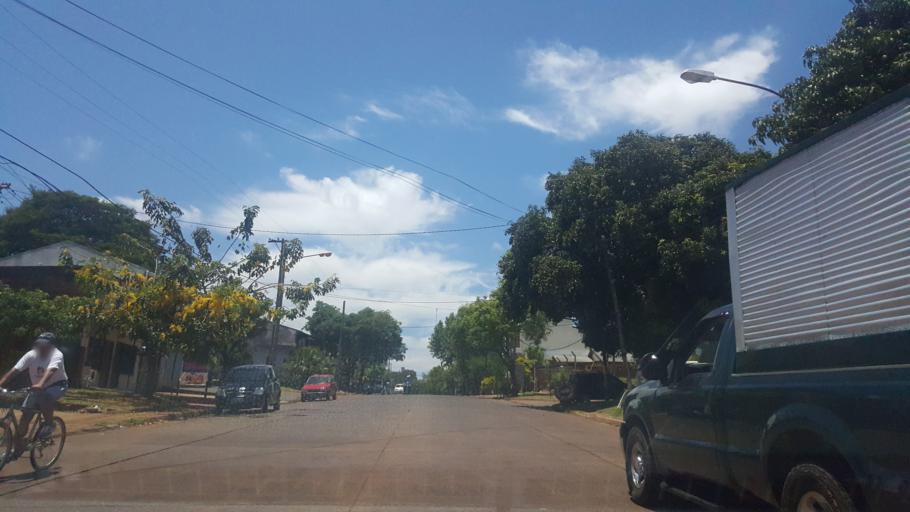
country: AR
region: Misiones
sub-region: Departamento de Capital
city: Posadas
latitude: -27.3675
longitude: -55.9296
